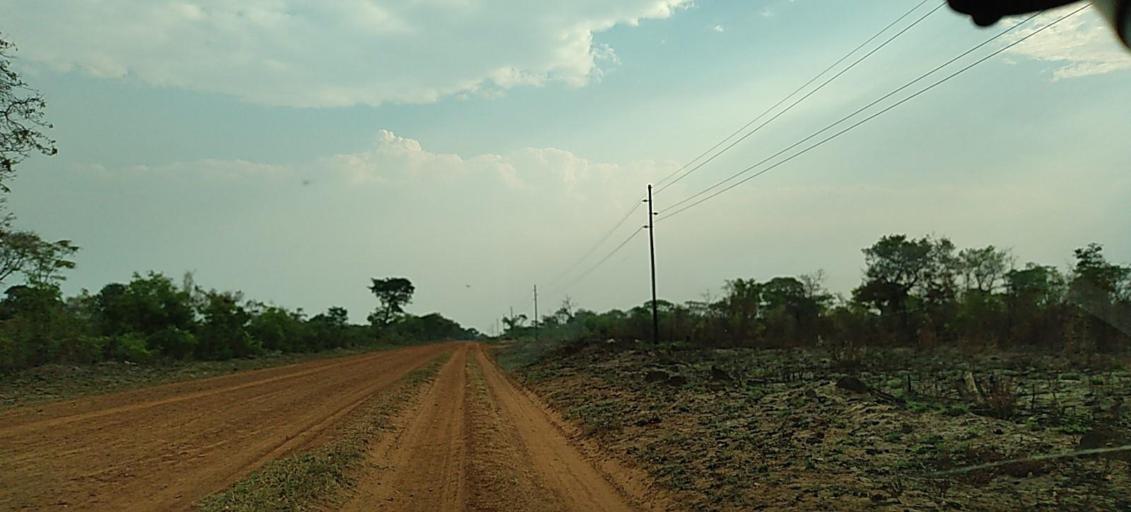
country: ZM
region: North-Western
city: Kabompo
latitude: -13.8952
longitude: 23.6579
